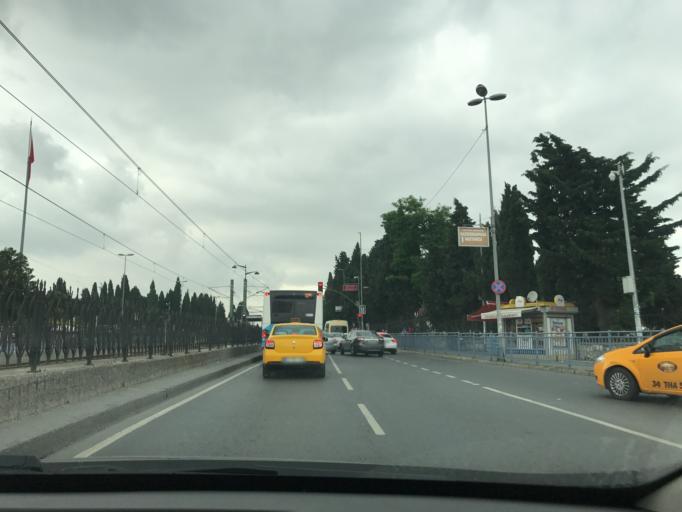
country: TR
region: Istanbul
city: Istanbul
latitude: 41.0338
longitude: 28.9296
